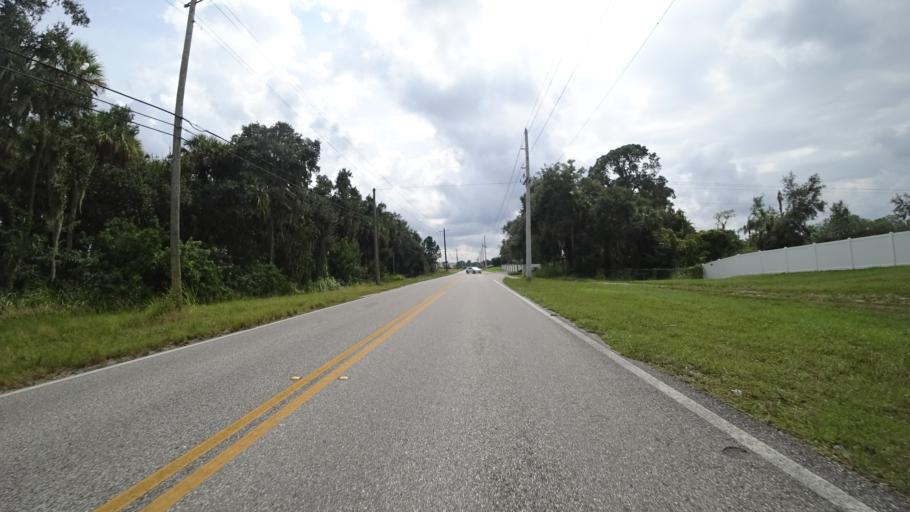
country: US
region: Florida
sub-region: Manatee County
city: Ellenton
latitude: 27.5469
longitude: -82.4787
